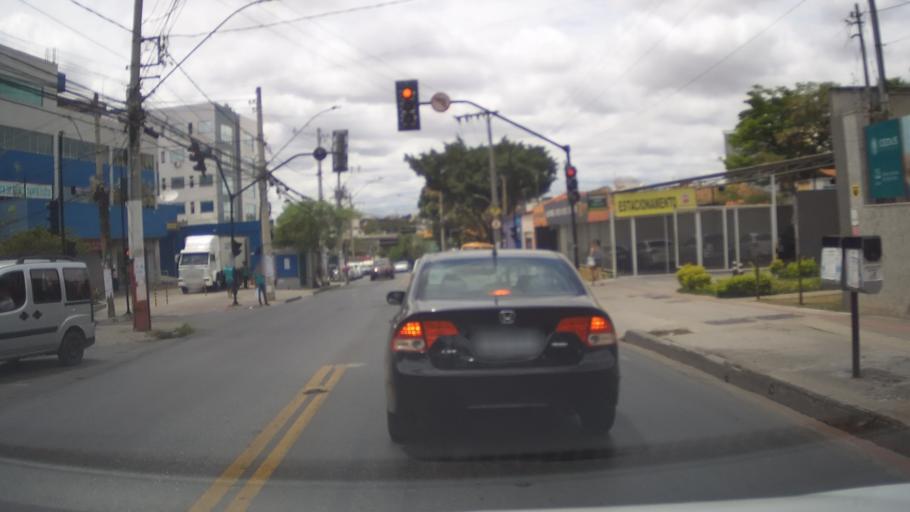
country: BR
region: Minas Gerais
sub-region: Belo Horizonte
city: Belo Horizonte
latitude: -19.8176
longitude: -43.9543
